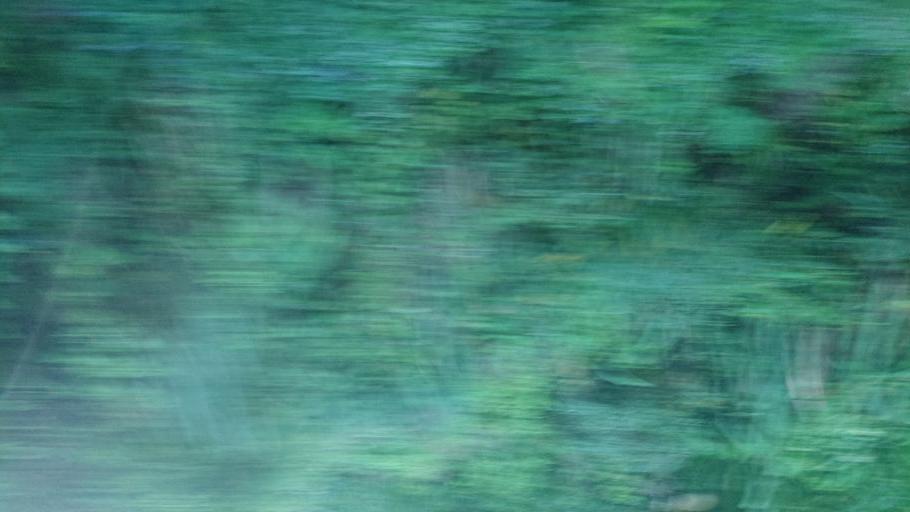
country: TW
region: Taiwan
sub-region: Chiayi
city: Jiayi Shi
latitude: 23.5348
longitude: 120.6292
